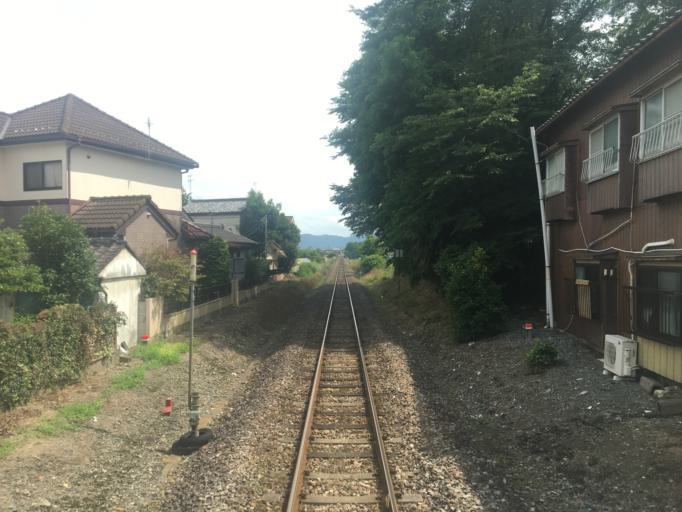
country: JP
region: Gunma
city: Fujioka
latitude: 36.2431
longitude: 139.0832
